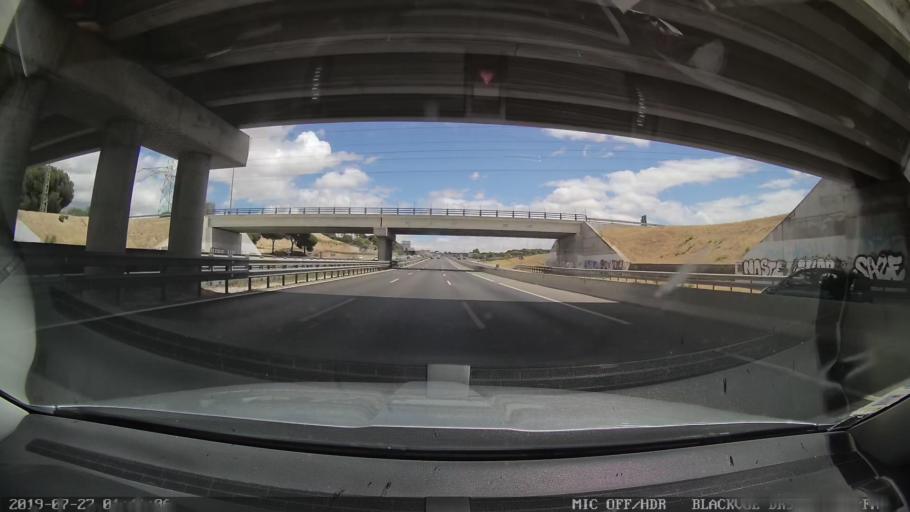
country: ES
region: Madrid
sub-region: Provincia de Madrid
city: Arroyomolinos
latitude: 40.3029
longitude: -3.9221
